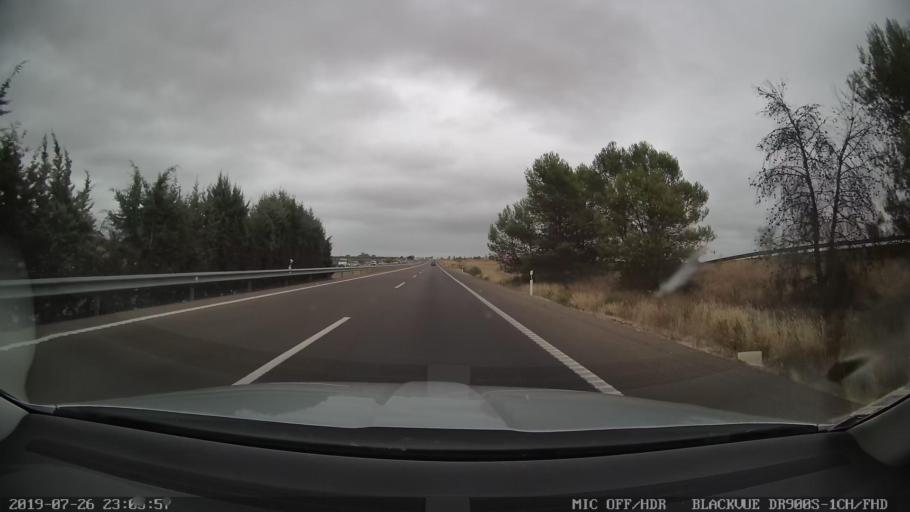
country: ES
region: Extremadura
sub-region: Provincia de Badajoz
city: San Pedro de Merida
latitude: 38.9502
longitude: -6.2189
